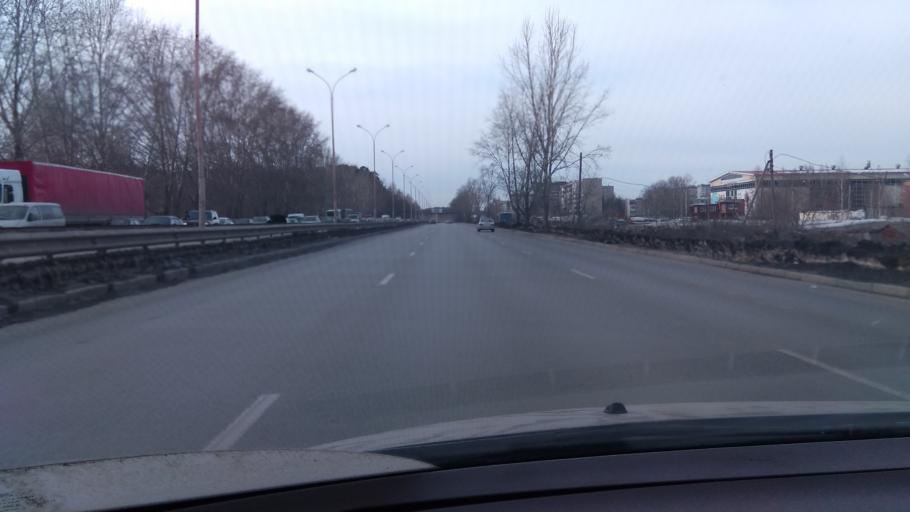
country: RU
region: Sverdlovsk
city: Sovkhoznyy
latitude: 56.7955
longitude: 60.5632
